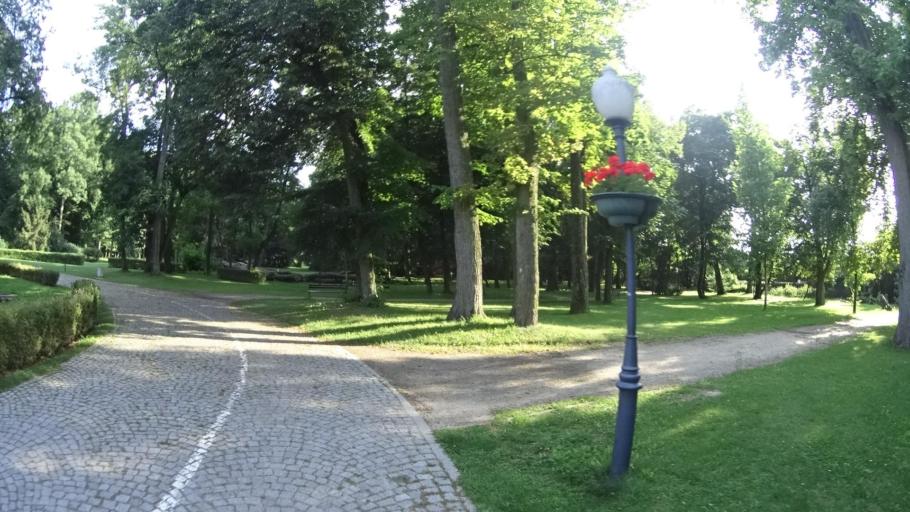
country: PL
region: Masovian Voivodeship
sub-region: Powiat pruszkowski
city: Nadarzyn
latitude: 52.0477
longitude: 20.7826
